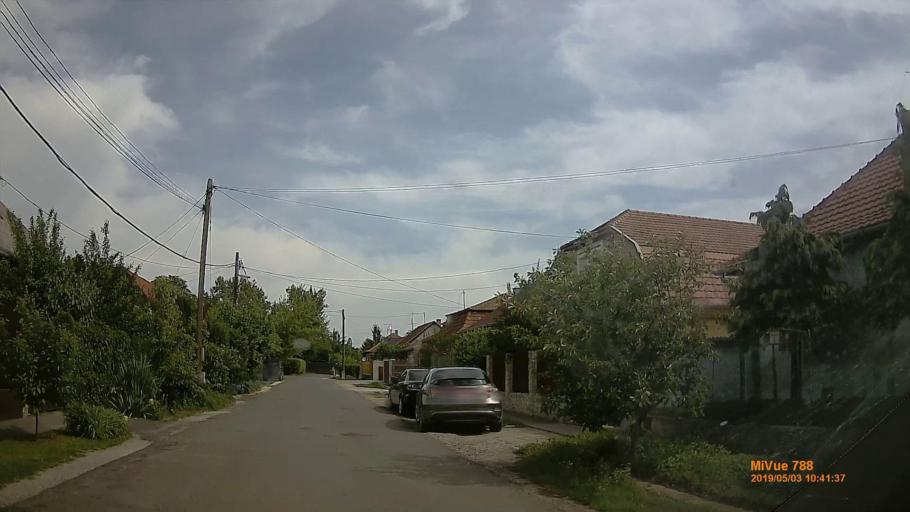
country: HU
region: Jasz-Nagykun-Szolnok
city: Szolnok
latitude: 47.1849
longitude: 20.1946
